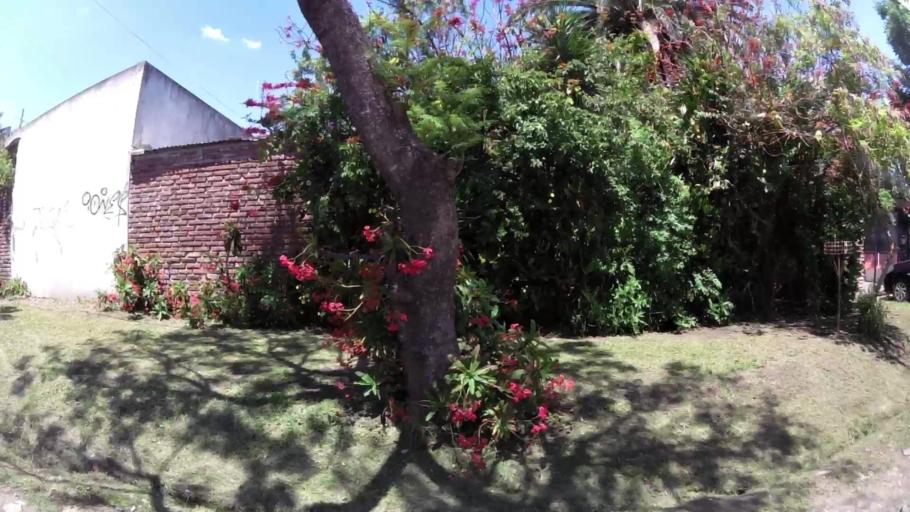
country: AR
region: Buenos Aires
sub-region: Partido de Merlo
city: Merlo
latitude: -34.6581
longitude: -58.6936
